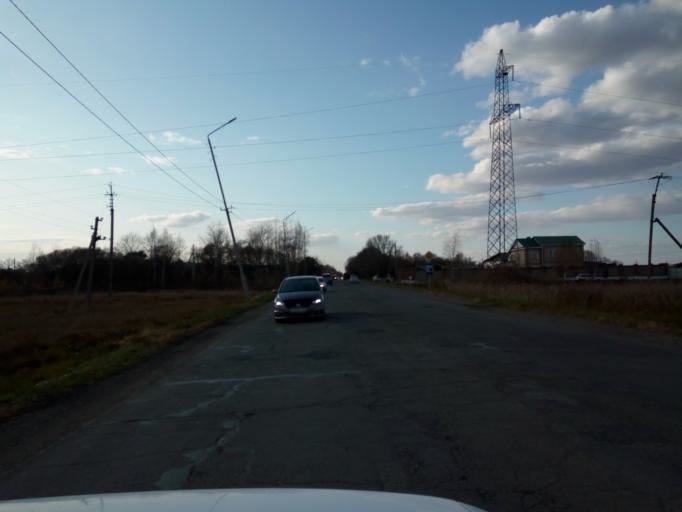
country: RU
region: Primorskiy
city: Dal'nerechensk
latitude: 45.9171
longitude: 133.7641
